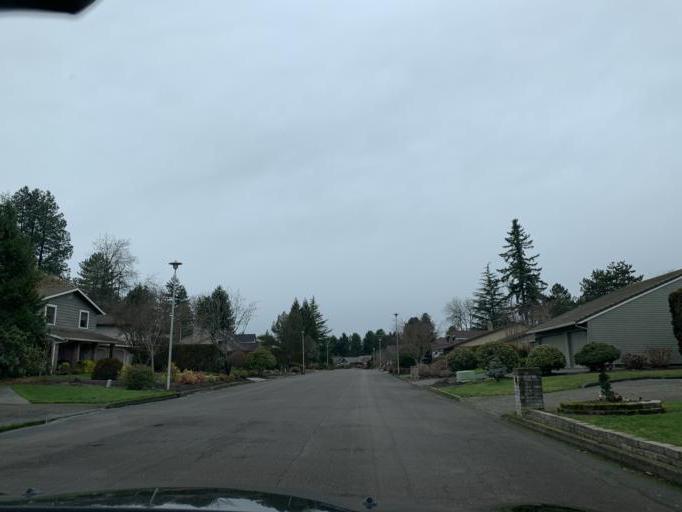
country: US
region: Washington
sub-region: Clark County
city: Walnut Grove
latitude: 45.6750
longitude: -122.5870
